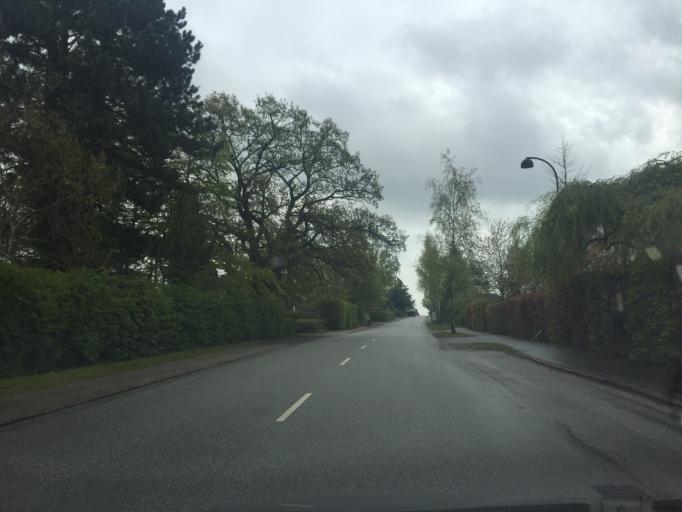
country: DK
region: Capital Region
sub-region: Rudersdal Kommune
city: Holte
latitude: 55.8015
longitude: 12.4519
